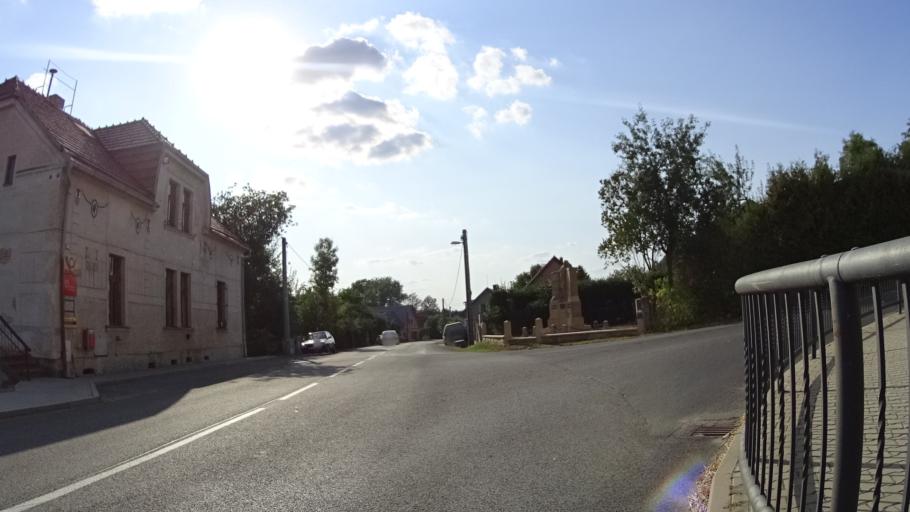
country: CZ
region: Central Bohemia
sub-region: Okres Mlada Boleslav
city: Zd'ar
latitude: 50.5432
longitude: 15.0837
